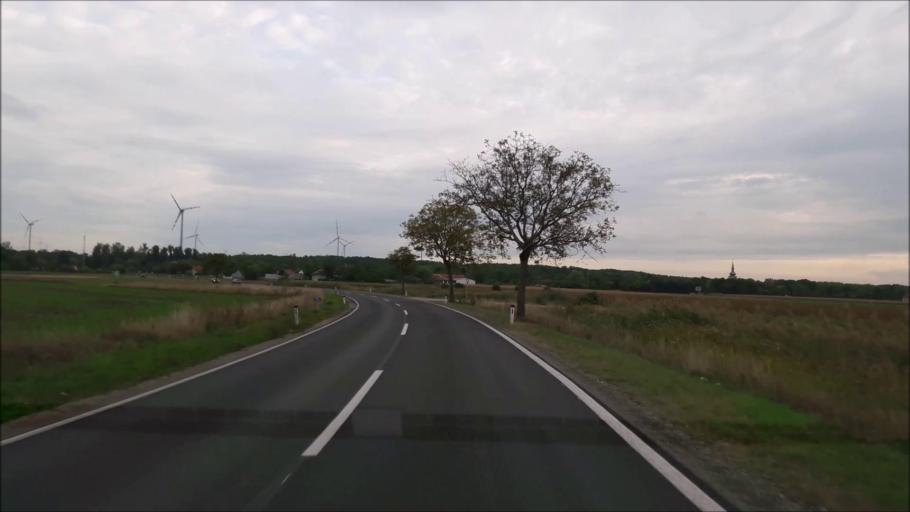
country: AT
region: Lower Austria
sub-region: Politischer Bezirk Bruck an der Leitha
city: Rohrau
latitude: 48.0742
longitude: 16.8607
